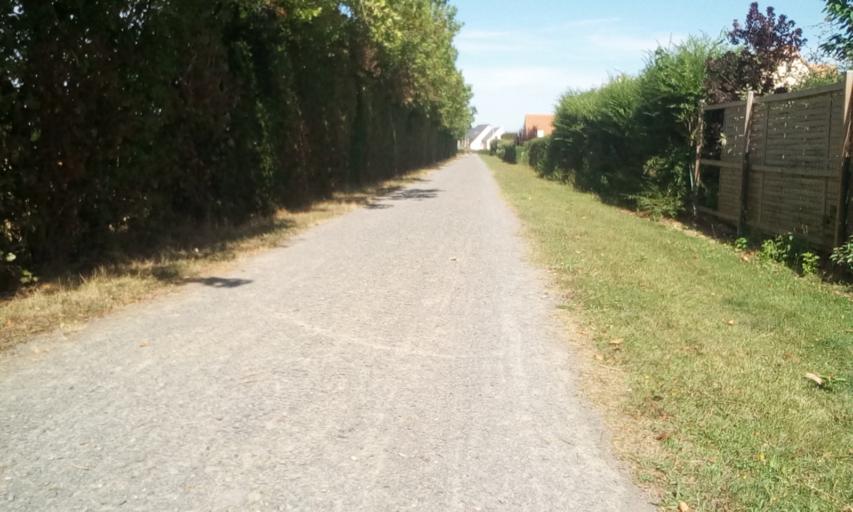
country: FR
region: Lower Normandy
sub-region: Departement du Calvados
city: Eterville
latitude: 49.1473
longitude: -0.4274
